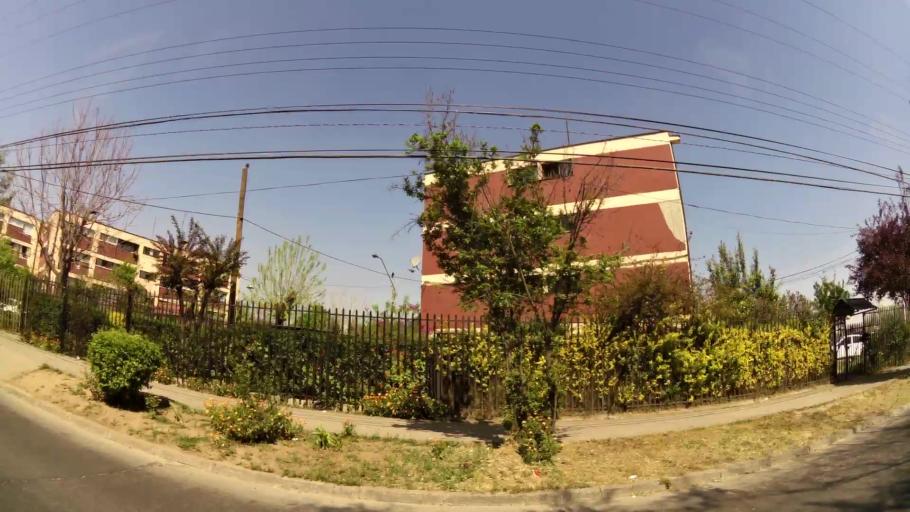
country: CL
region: Santiago Metropolitan
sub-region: Provincia de Santiago
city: Villa Presidente Frei, Nunoa, Santiago, Chile
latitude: -33.4734
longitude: -70.5840
